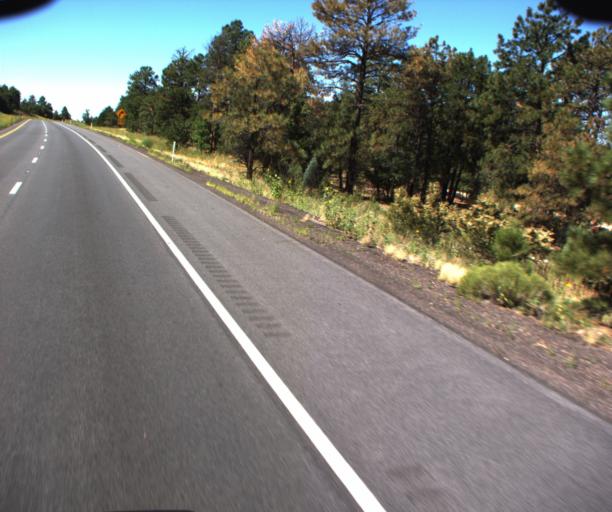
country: US
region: Arizona
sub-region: Coconino County
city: Williams
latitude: 35.2301
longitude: -112.2346
